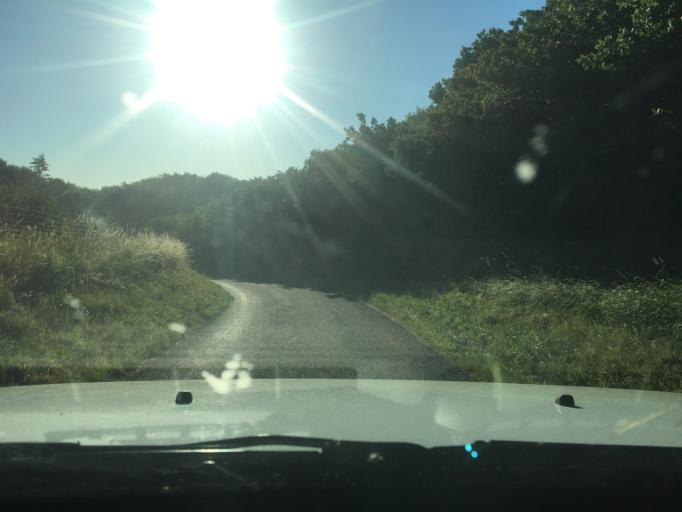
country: DK
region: Central Jutland
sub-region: Favrskov Kommune
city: Hadsten
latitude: 56.3949
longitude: 10.0768
